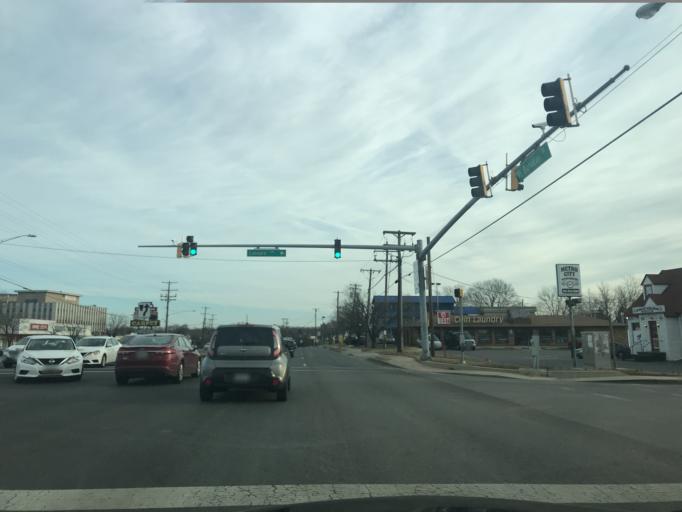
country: US
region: Maryland
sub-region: Prince George's County
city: Marlow Heights
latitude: 38.8285
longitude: -76.9429
